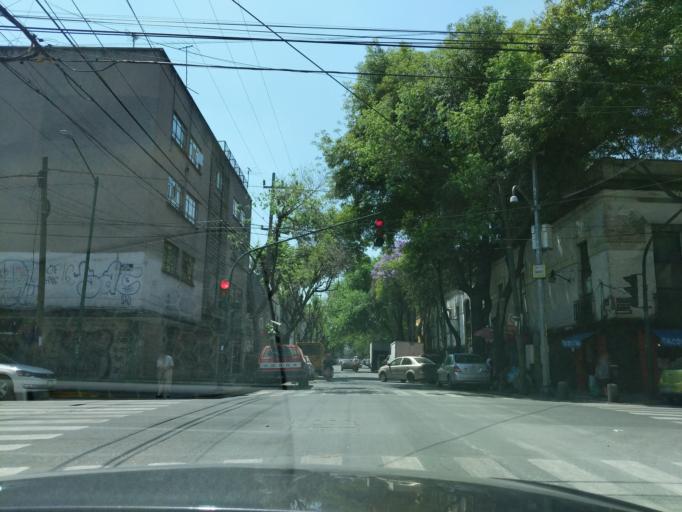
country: MX
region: Mexico City
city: Cuauhtemoc
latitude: 19.4464
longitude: -99.1629
